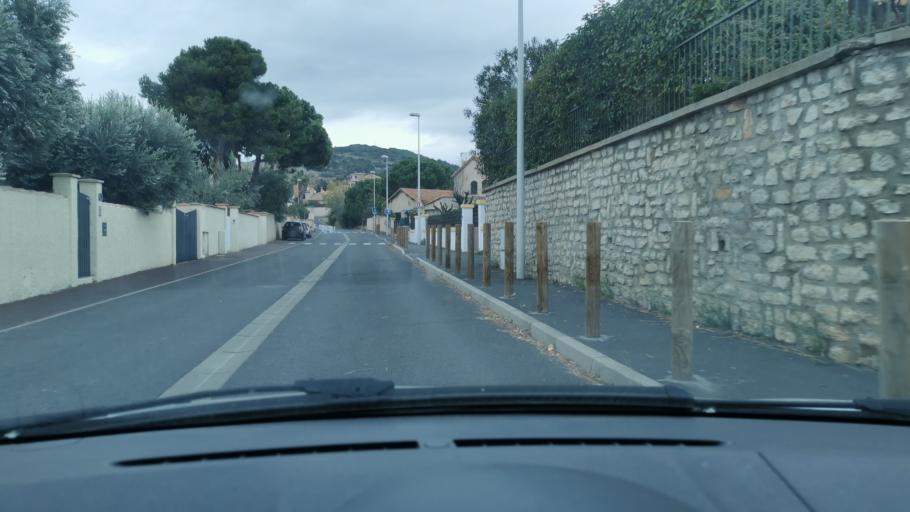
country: FR
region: Languedoc-Roussillon
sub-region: Departement de l'Herault
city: Frontignan
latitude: 43.4537
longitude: 3.7541
